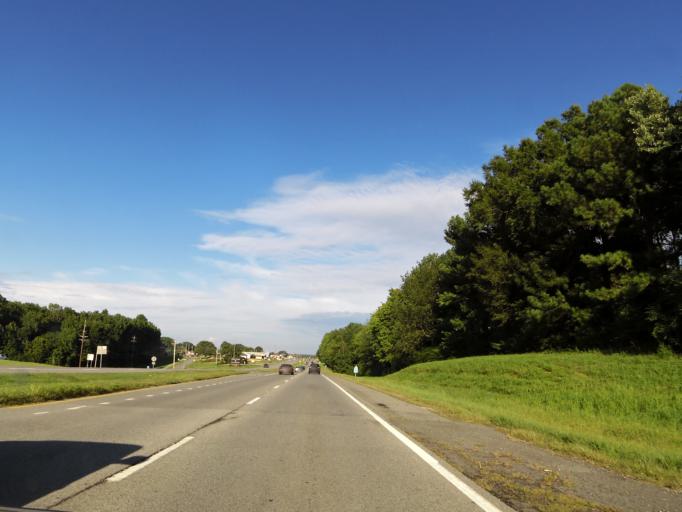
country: US
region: Alabama
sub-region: Lauderdale County
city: Killen
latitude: 34.8562
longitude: -87.5508
